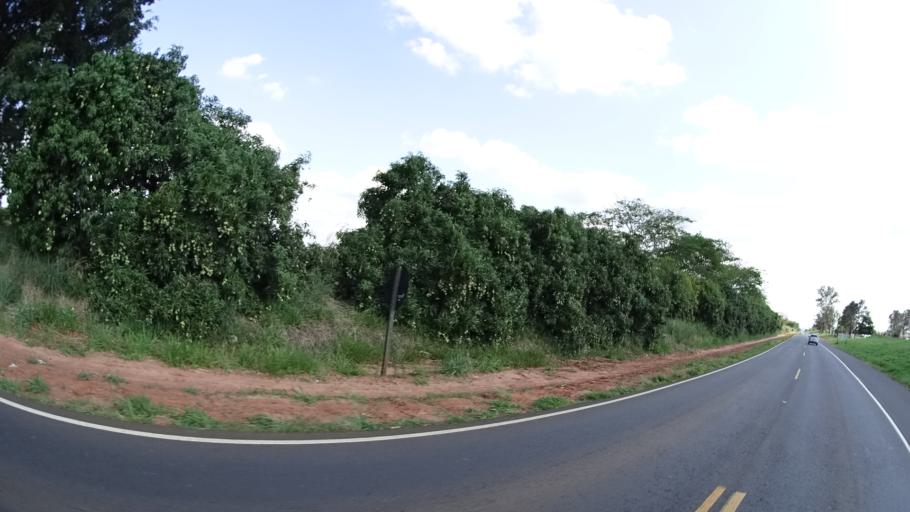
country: BR
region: Sao Paulo
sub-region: Guapiacu
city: Guapiacu
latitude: -20.9951
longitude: -49.2099
